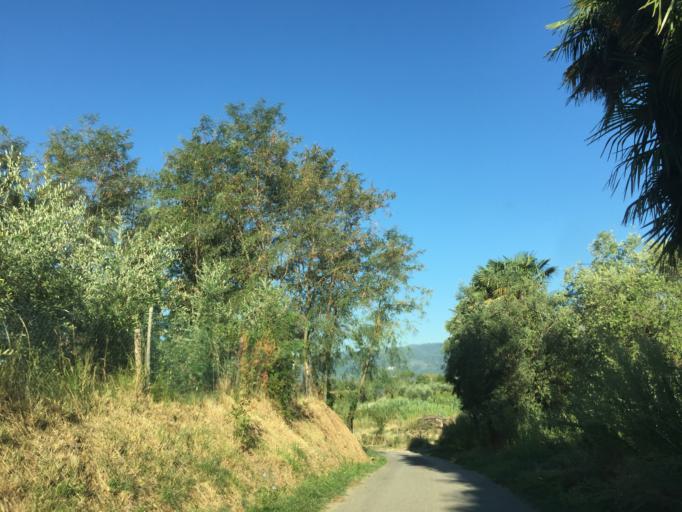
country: IT
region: Tuscany
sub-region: Provincia di Pistoia
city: Pistoia
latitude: 43.9482
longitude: 10.9469
